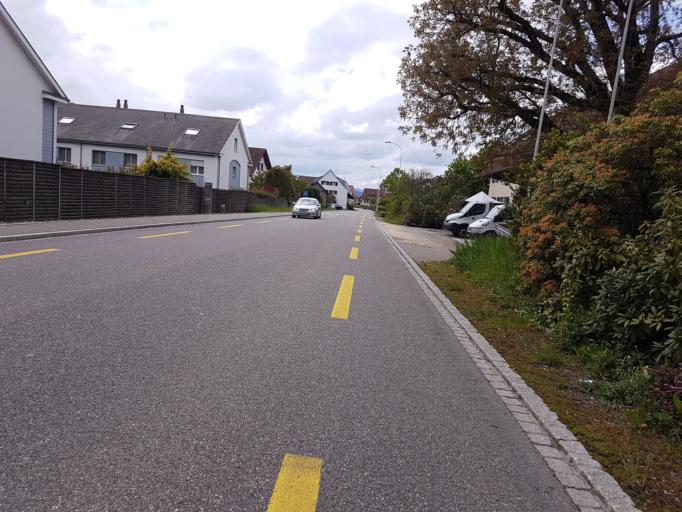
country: CH
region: Aargau
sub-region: Bezirk Baden
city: Wurenlingen
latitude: 47.5365
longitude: 8.2570
